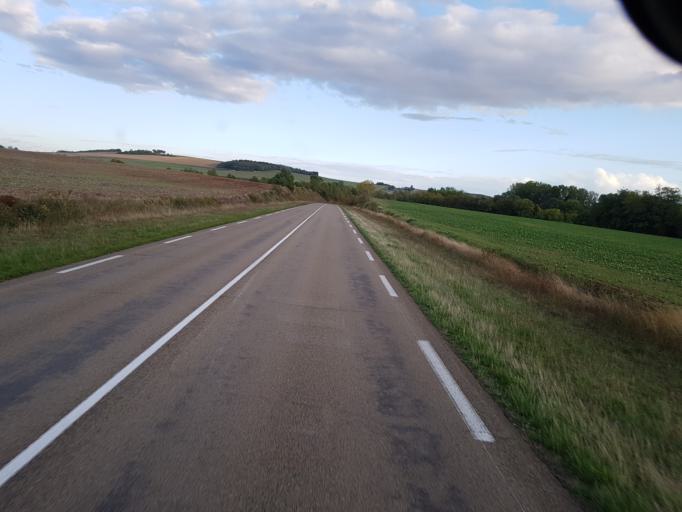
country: FR
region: Bourgogne
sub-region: Departement de l'Yonne
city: Sergines
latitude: 48.2836
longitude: 3.2652
